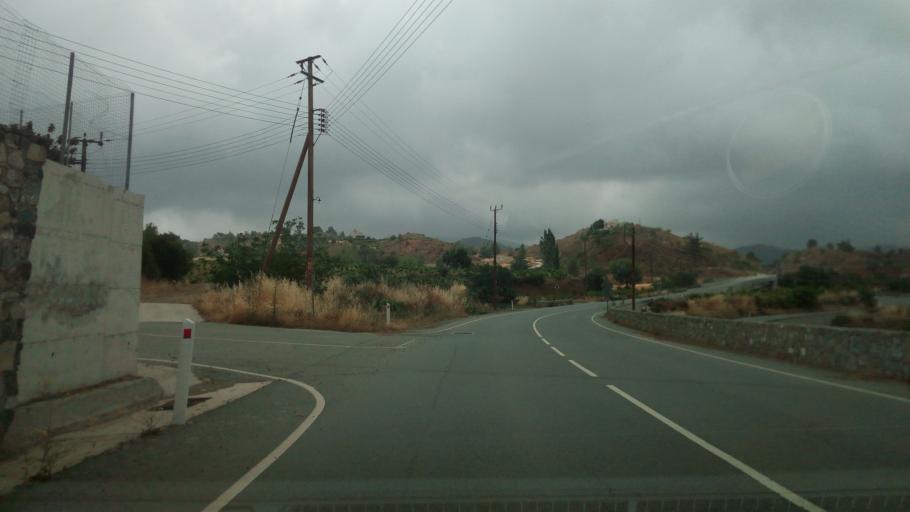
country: CY
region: Limassol
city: Pelendri
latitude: 34.8524
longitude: 33.0110
